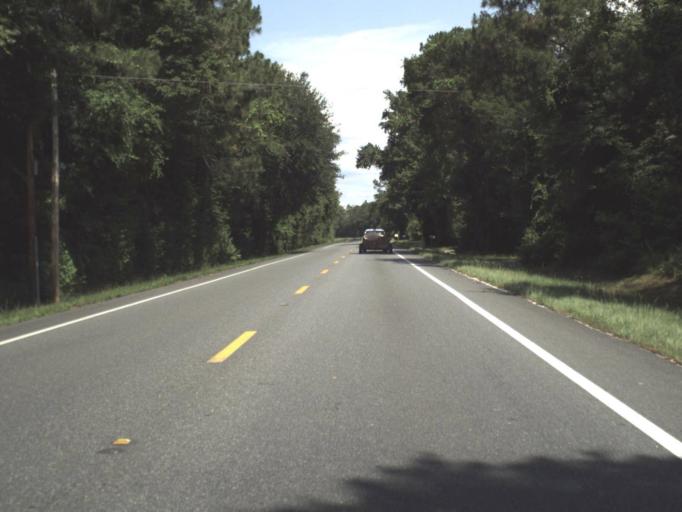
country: US
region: Florida
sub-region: Putnam County
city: Palatka
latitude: 29.6703
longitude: -81.7033
